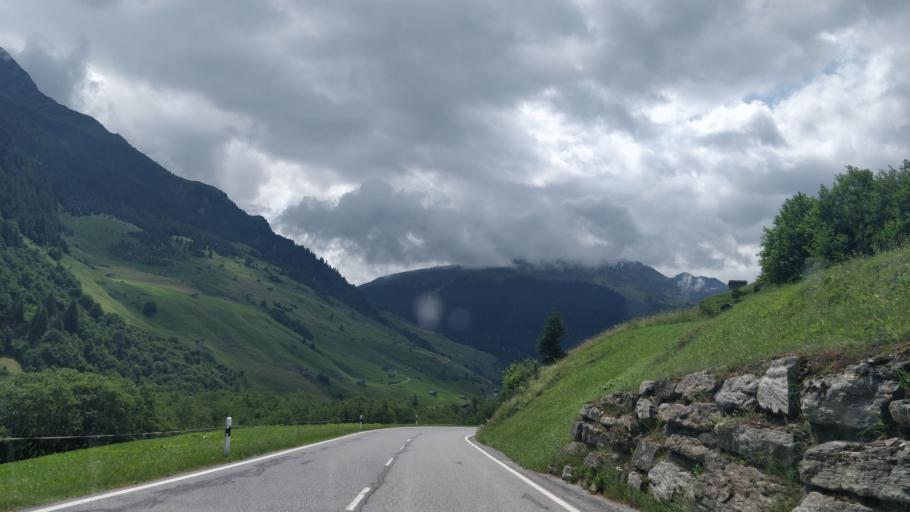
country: CH
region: Grisons
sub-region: Hinterrhein District
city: Hinterrhein
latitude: 46.6321
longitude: 9.1875
